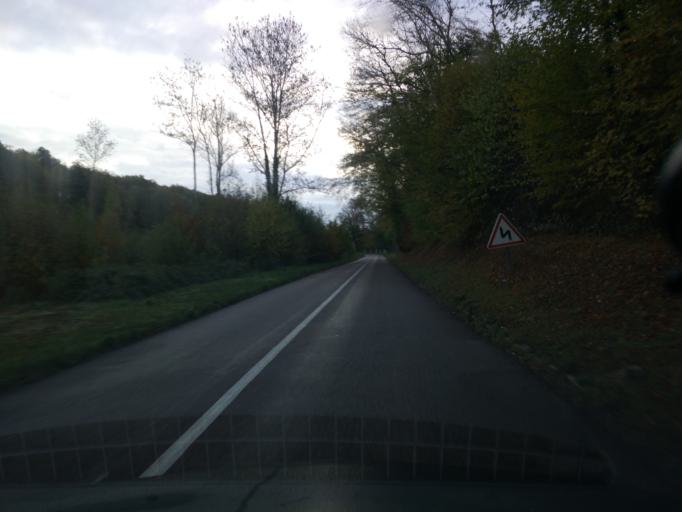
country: FR
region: Ile-de-France
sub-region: Departement de l'Essonne
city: Les Molieres
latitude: 48.6837
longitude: 2.0701
